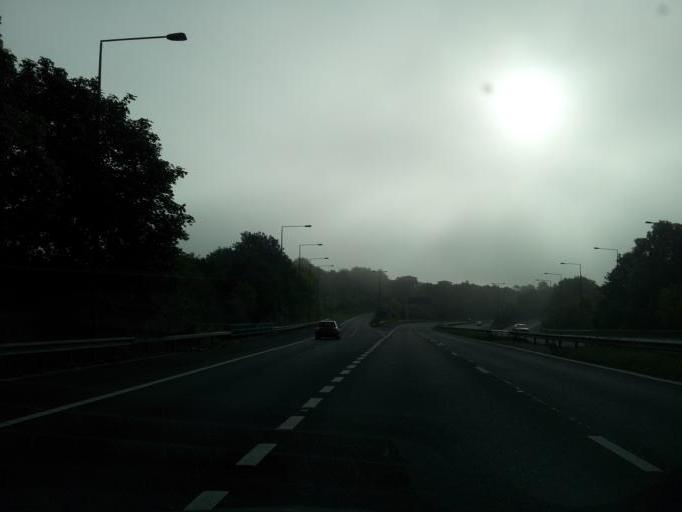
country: GB
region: England
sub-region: Borough of Oldham
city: Royton
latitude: 53.5603
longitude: -2.1455
